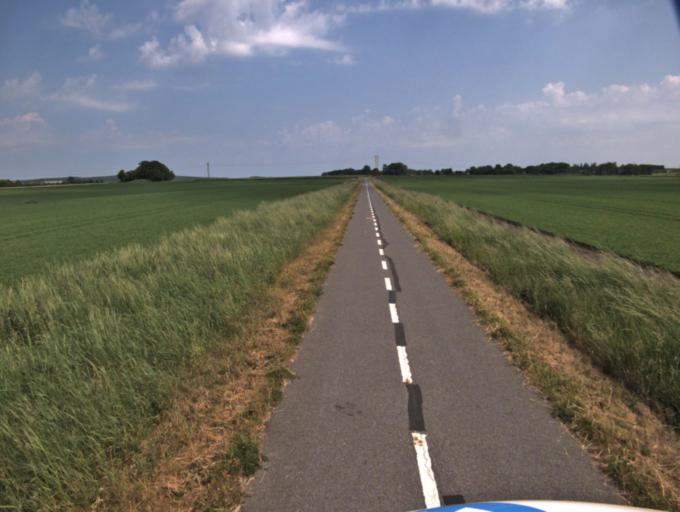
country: SE
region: Skane
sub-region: Kristianstads Kommun
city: Kristianstad
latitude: 56.0663
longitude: 14.1914
